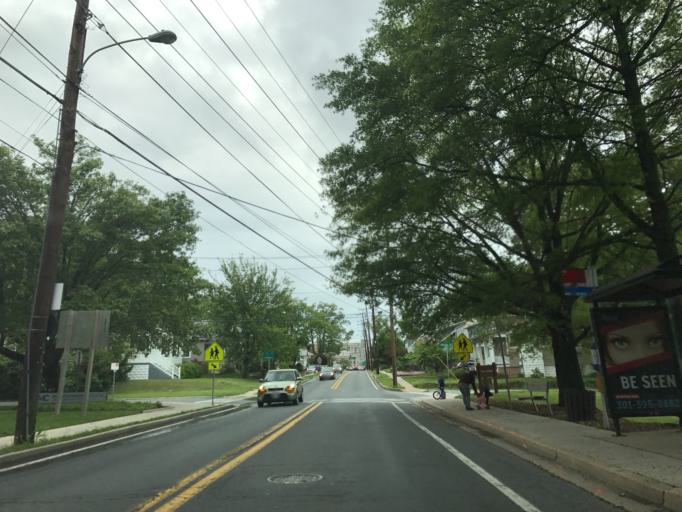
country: US
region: Maryland
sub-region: Montgomery County
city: Silver Spring
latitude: 38.9864
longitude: -77.0210
